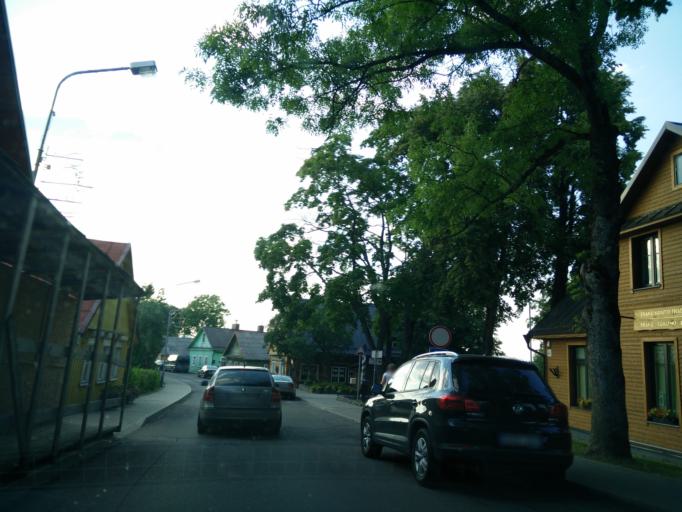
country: LT
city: Trakai
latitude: 54.6484
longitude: 24.9324
